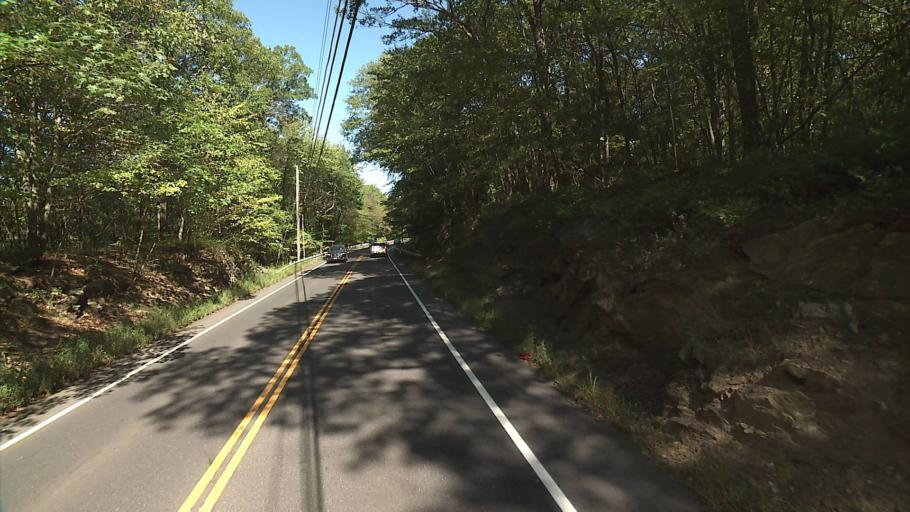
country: US
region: Connecticut
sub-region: New Haven County
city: Prospect
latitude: 41.4532
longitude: -72.9684
